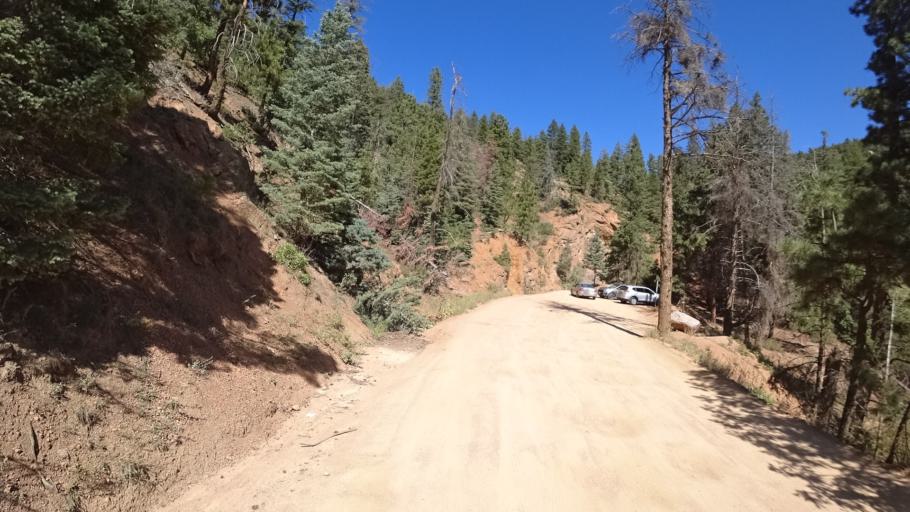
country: US
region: Colorado
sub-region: El Paso County
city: Manitou Springs
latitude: 38.7935
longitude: -104.8981
